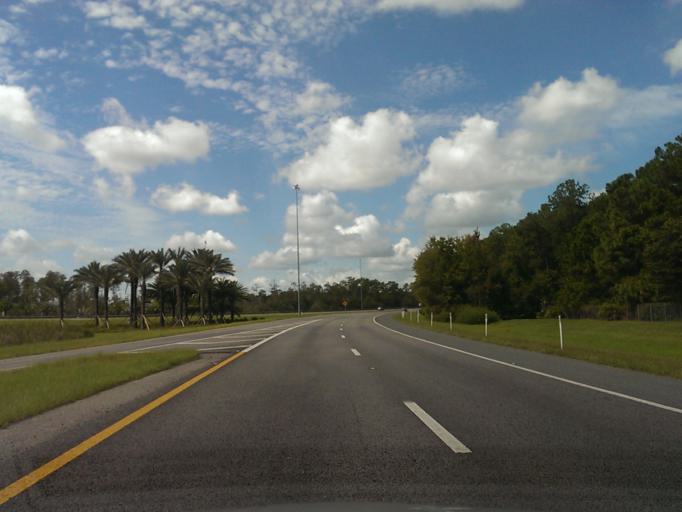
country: US
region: Florida
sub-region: Osceola County
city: Celebration
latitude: 28.3338
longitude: -81.5472
